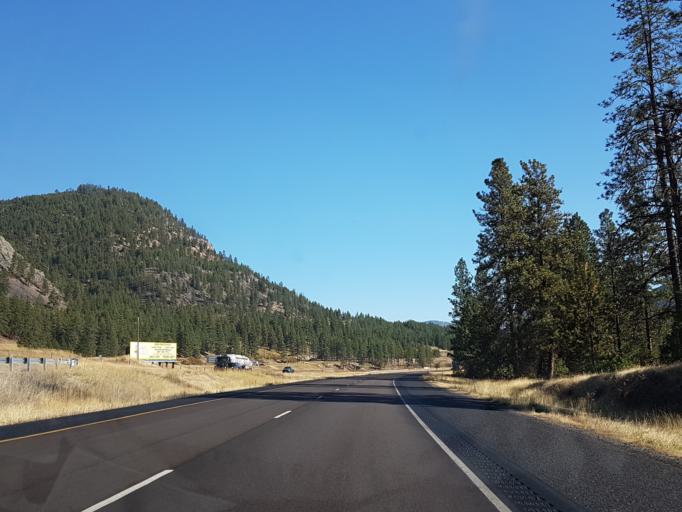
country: US
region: Montana
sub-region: Missoula County
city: Frenchtown
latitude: 47.0177
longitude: -114.5111
